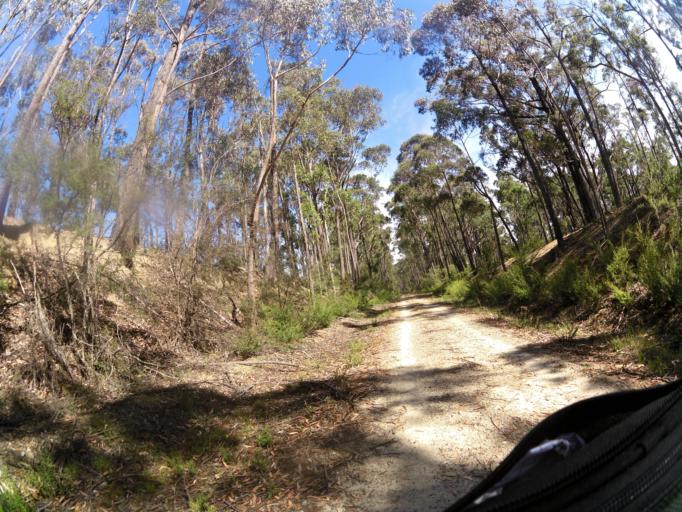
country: AU
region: Victoria
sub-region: East Gippsland
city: Lakes Entrance
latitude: -37.7209
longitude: 148.1454
